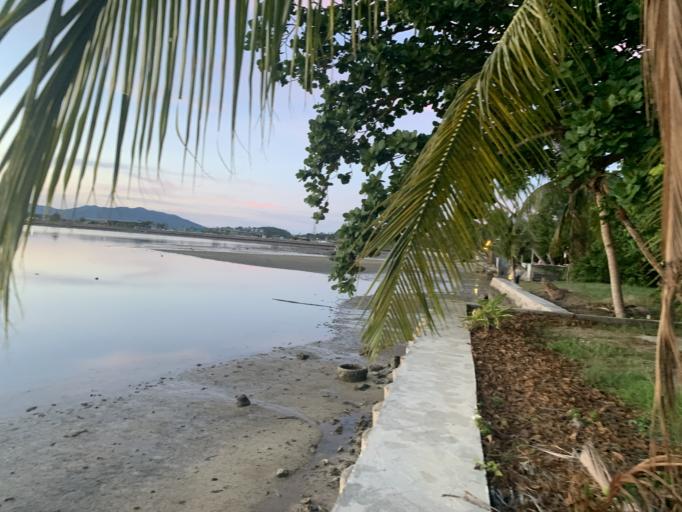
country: TH
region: Surat Thani
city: Ko Samui
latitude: 9.5715
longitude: 100.0635
